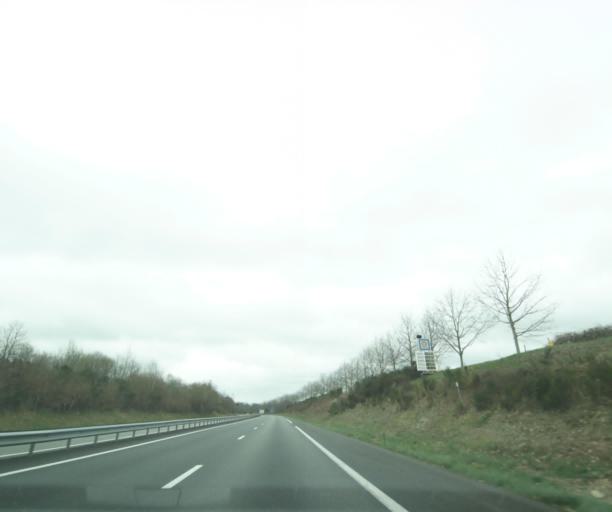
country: FR
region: Limousin
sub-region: Departement de la Haute-Vienne
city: Saint-Sulpice-les-Feuilles
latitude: 46.3247
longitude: 1.4176
